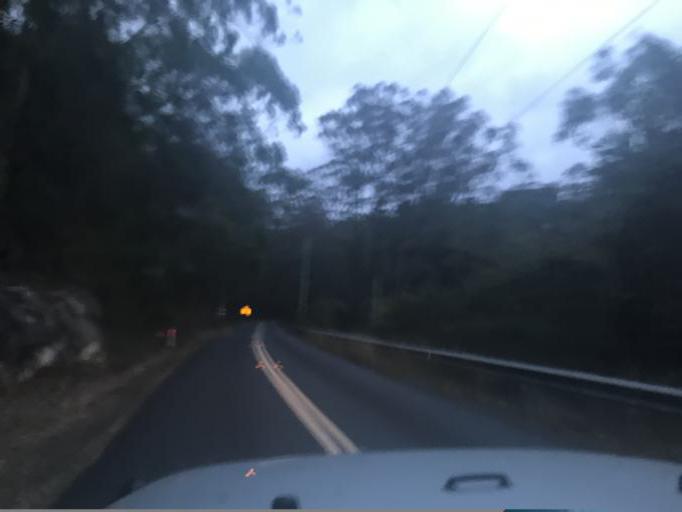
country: AU
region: New South Wales
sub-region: Hawkesbury
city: Pitt Town
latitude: -33.4764
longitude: 150.8696
